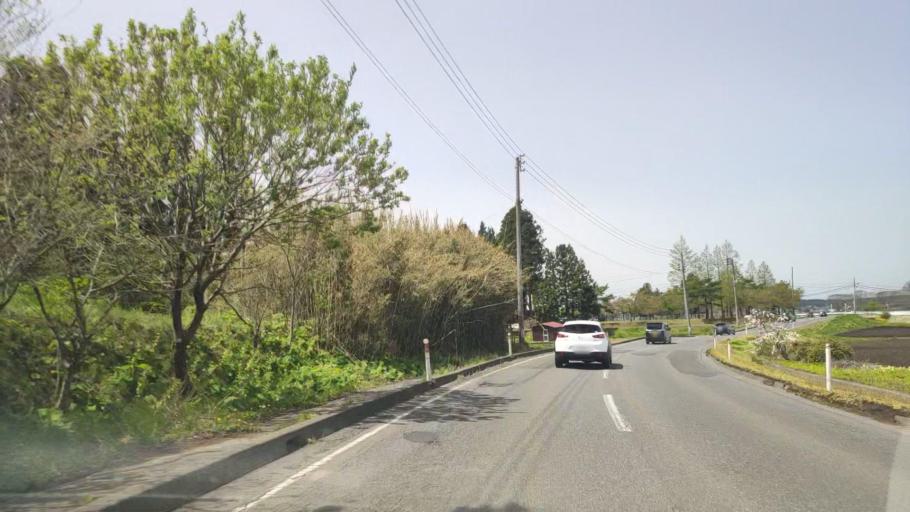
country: JP
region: Aomori
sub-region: Misawa Shi
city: Inuotose
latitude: 40.5926
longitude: 141.3433
